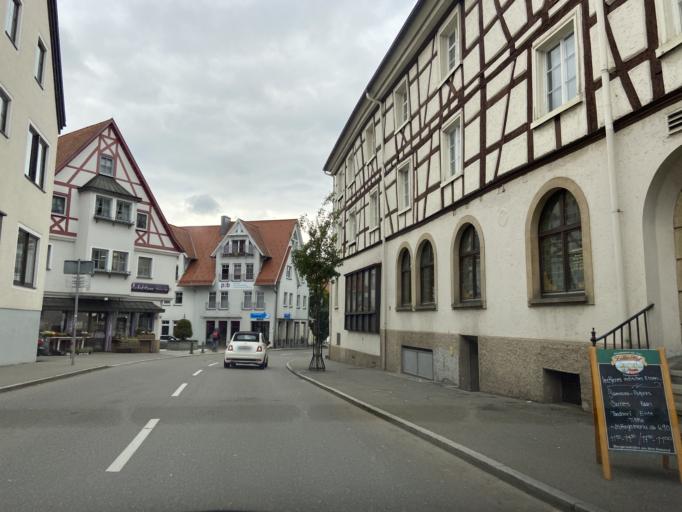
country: DE
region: Baden-Wuerttemberg
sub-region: Tuebingen Region
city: Sigmaringen
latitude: 48.0869
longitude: 9.2146
